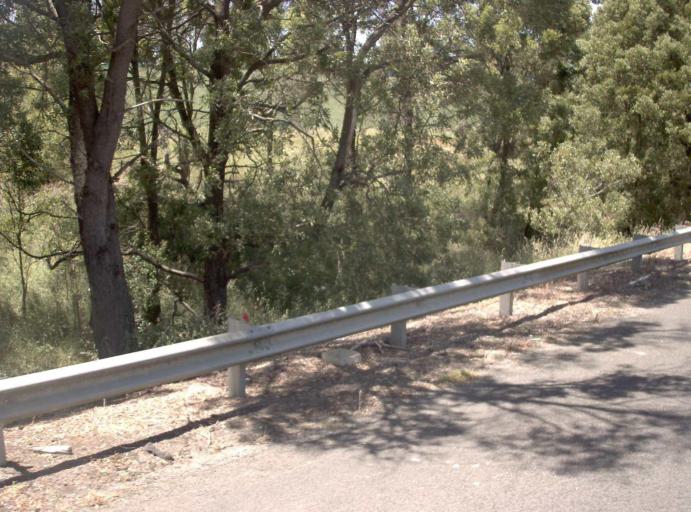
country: AU
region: Victoria
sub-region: Baw Baw
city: Warragul
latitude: -38.1492
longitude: 145.8877
